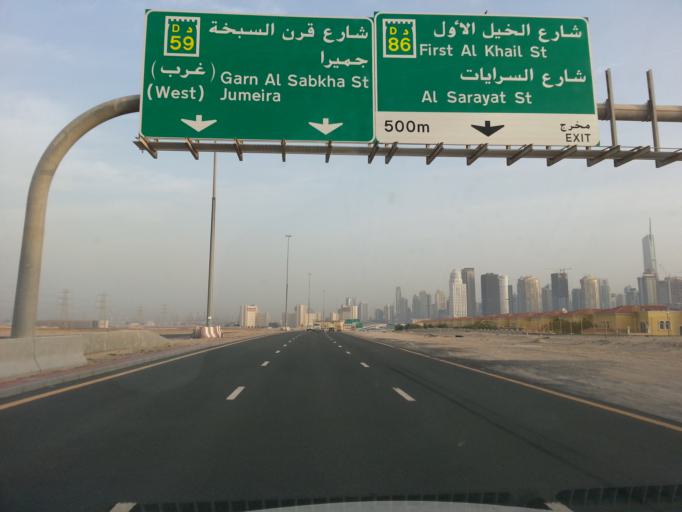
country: AE
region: Dubai
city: Dubai
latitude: 25.0500
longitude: 55.1448
